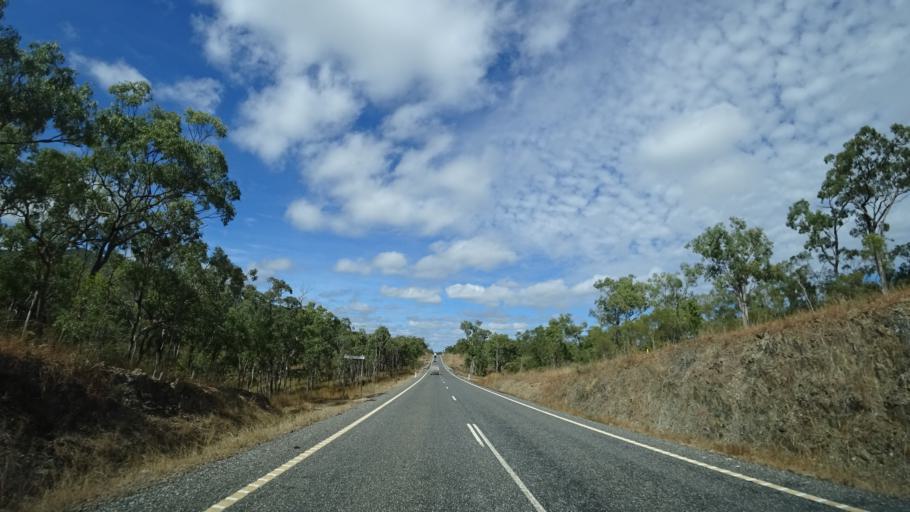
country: AU
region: Queensland
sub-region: Cairns
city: Port Douglas
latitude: -16.3235
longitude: 144.7198
